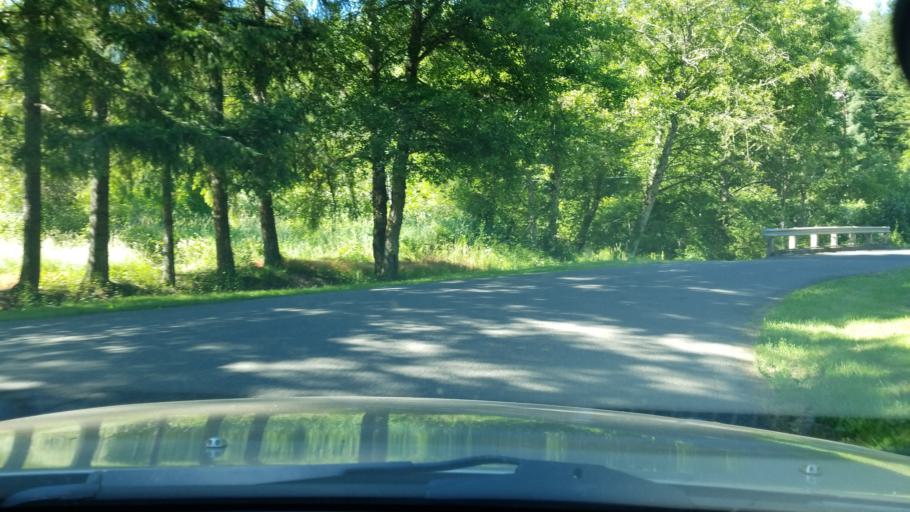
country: US
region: Oregon
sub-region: Yamhill County
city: McMinnville
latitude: 45.2261
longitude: -123.2700
